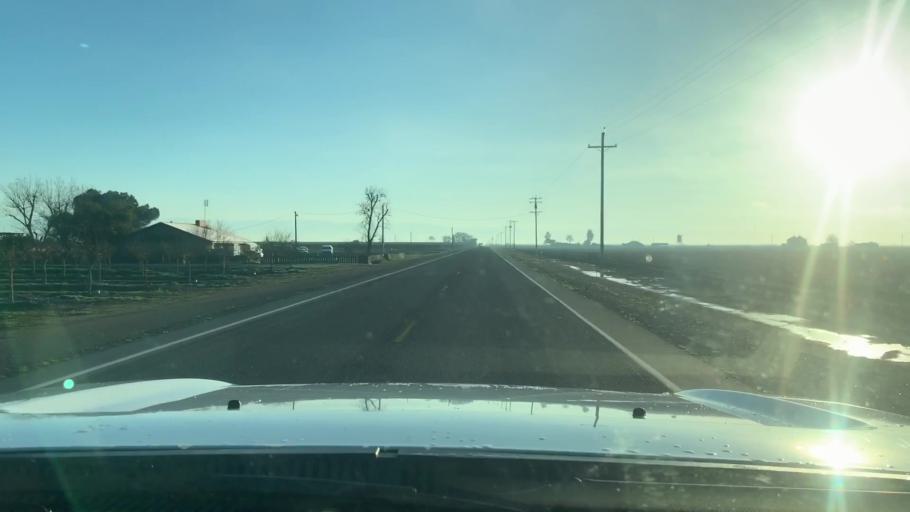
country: US
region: California
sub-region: Kings County
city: Home Garden
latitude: 36.2109
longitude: -119.5907
